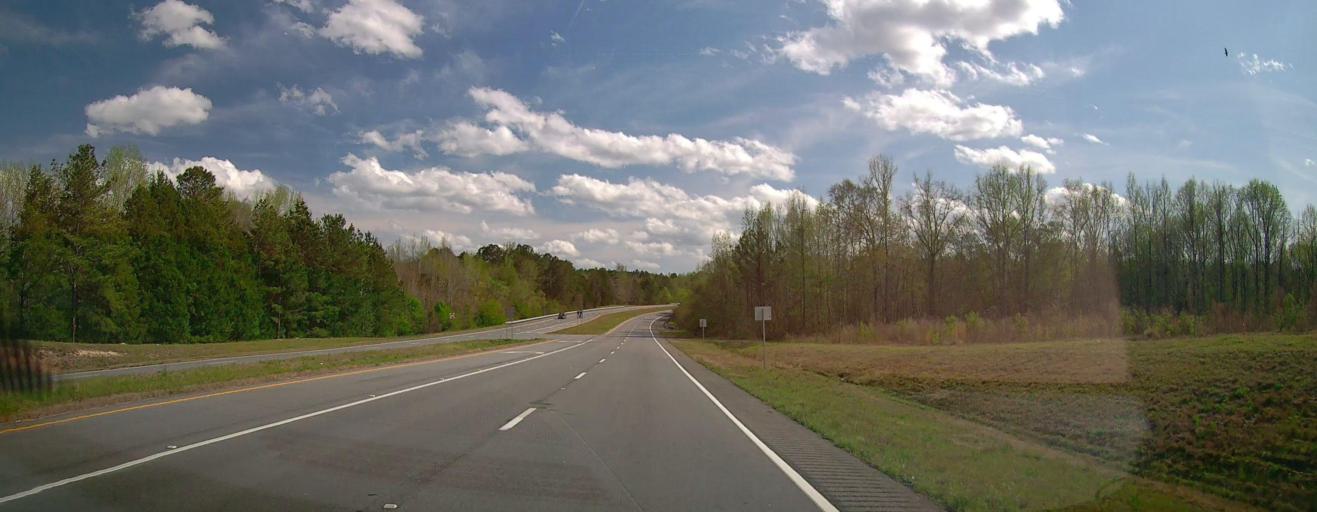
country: US
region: Georgia
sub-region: Baldwin County
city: Hardwick
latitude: 32.9883
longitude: -83.2125
